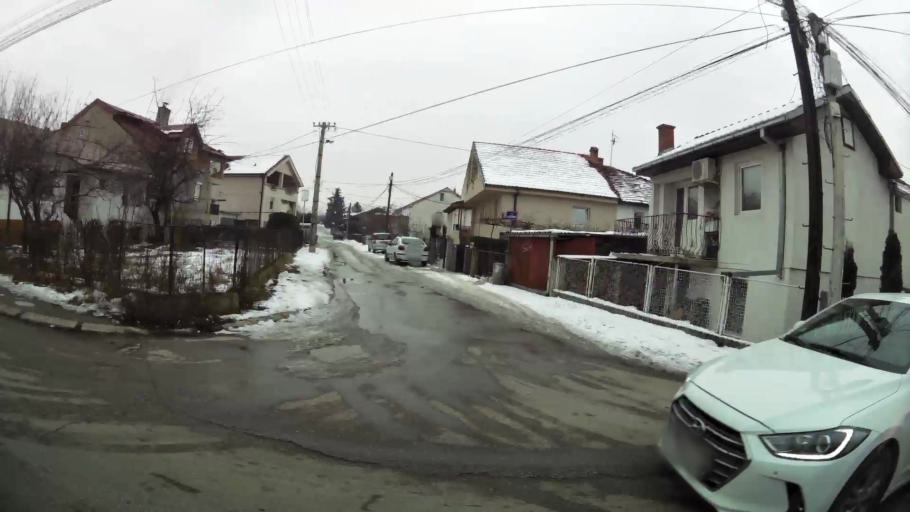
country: MK
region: Butel
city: Butel
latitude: 42.0361
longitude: 21.4491
